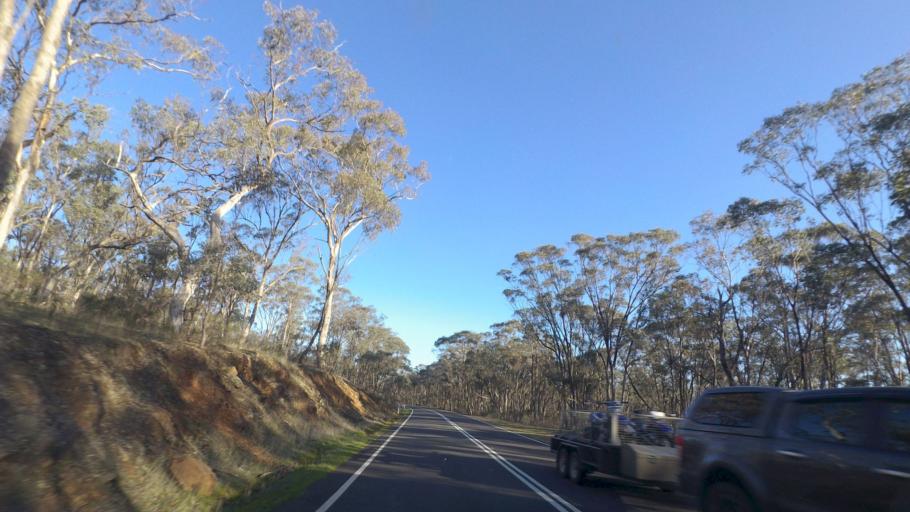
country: AU
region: Victoria
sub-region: Greater Bendigo
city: Kennington
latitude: -36.9170
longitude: 144.4919
